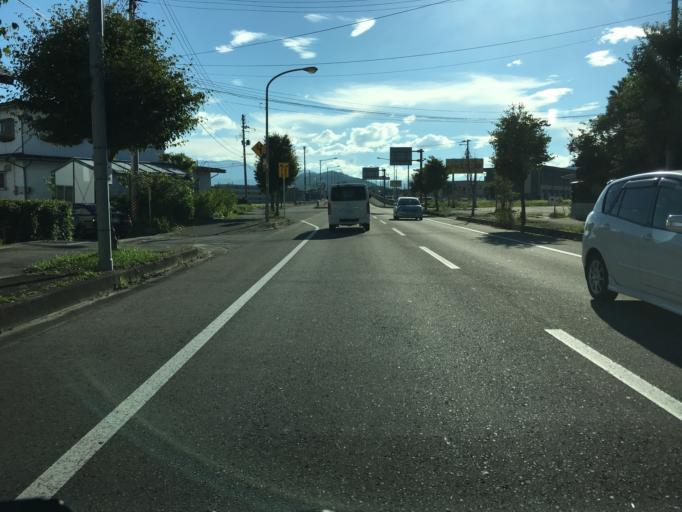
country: JP
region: Yamagata
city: Yonezawa
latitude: 37.9217
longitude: 140.0878
